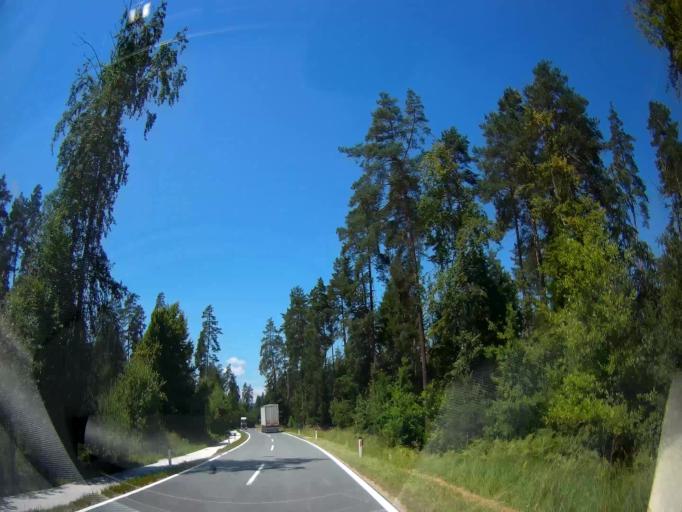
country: AT
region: Carinthia
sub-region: Politischer Bezirk Volkermarkt
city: Eberndorf
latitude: 46.6188
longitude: 14.6559
